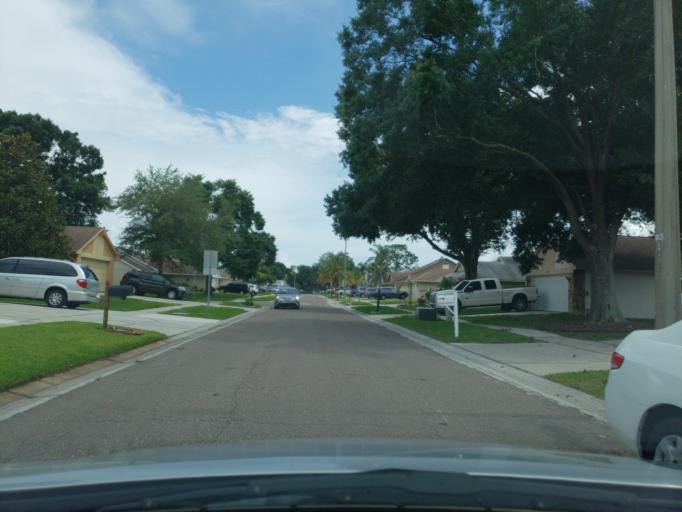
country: US
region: Florida
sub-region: Hillsborough County
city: Town 'n' Country
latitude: 28.0317
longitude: -82.5587
